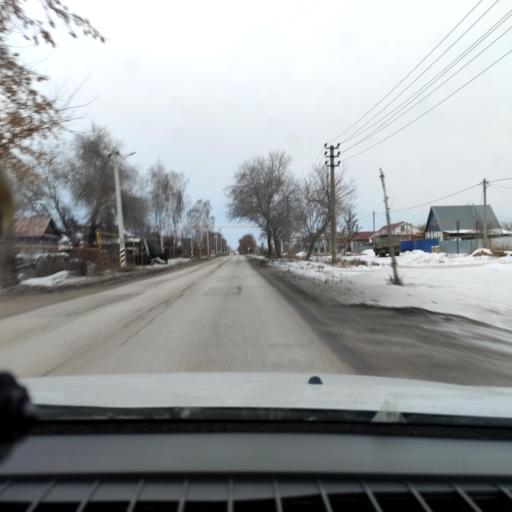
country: RU
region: Samara
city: Chapayevsk
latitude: 52.9996
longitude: 49.7179
